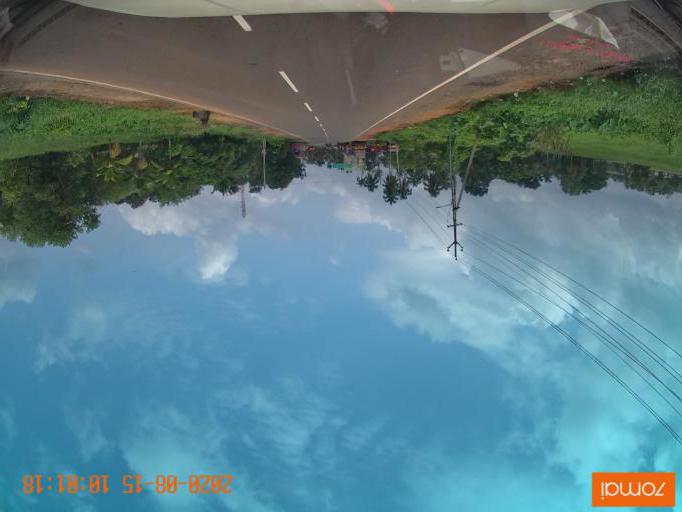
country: IN
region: Kerala
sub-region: Kottayam
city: Changanacheri
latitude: 9.4311
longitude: 76.5455
